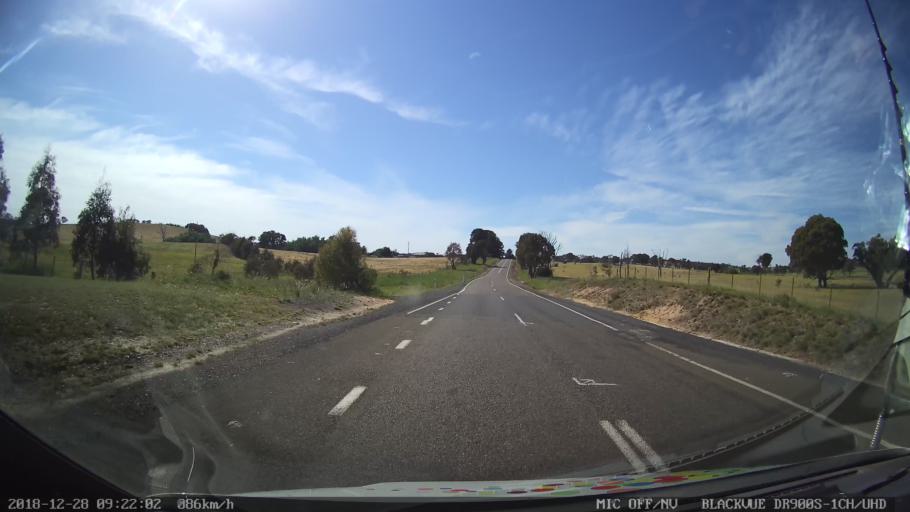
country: AU
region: New South Wales
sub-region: Upper Lachlan Shire
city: Crookwell
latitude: -34.3693
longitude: 149.3782
